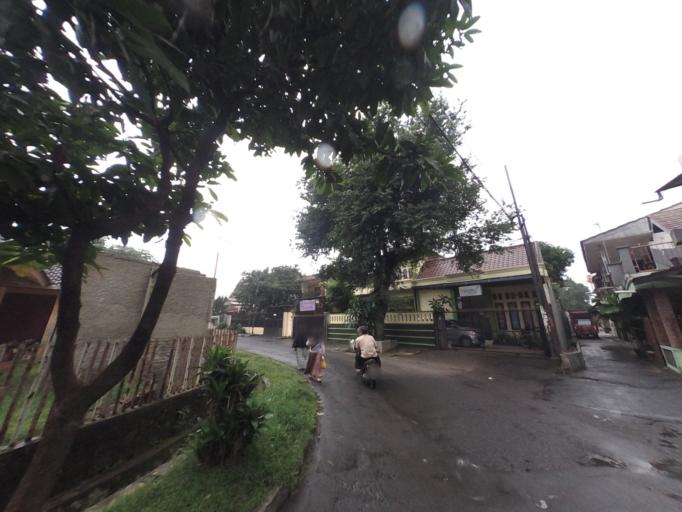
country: ID
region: West Java
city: Bogor
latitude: -6.5695
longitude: 106.7945
